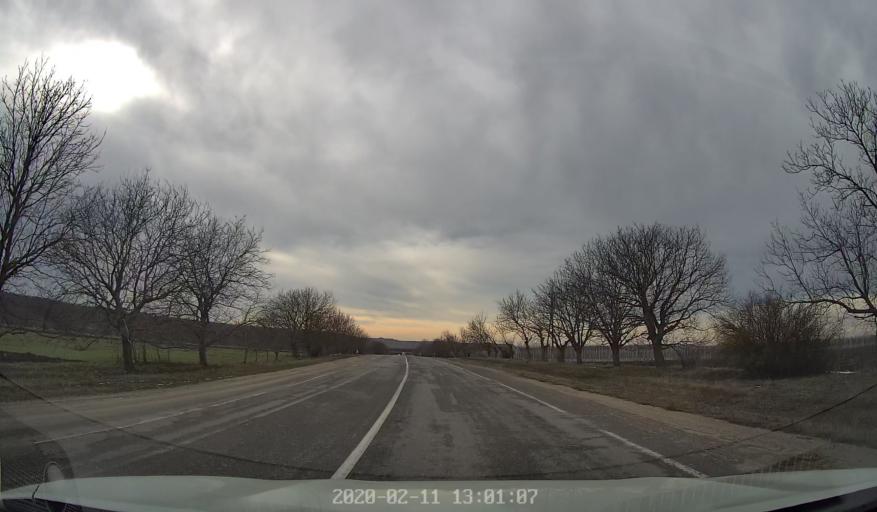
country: MD
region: Briceni
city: Briceni
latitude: 48.3214
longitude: 27.0076
